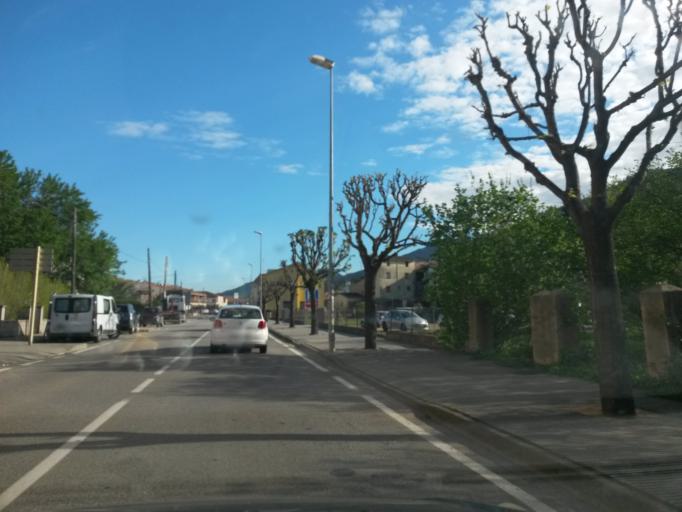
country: ES
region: Catalonia
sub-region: Provincia de Girona
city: la Cellera de Ter
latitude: 42.0075
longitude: 2.6050
